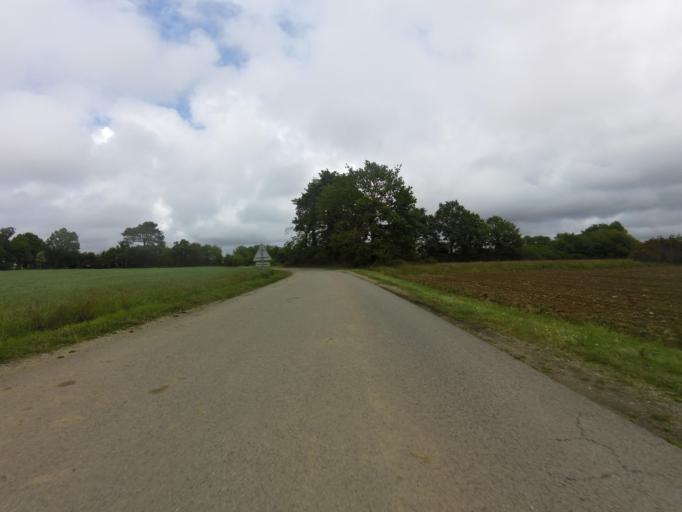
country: FR
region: Brittany
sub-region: Departement du Morbihan
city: Plougoumelen
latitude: 47.6380
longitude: -2.9012
